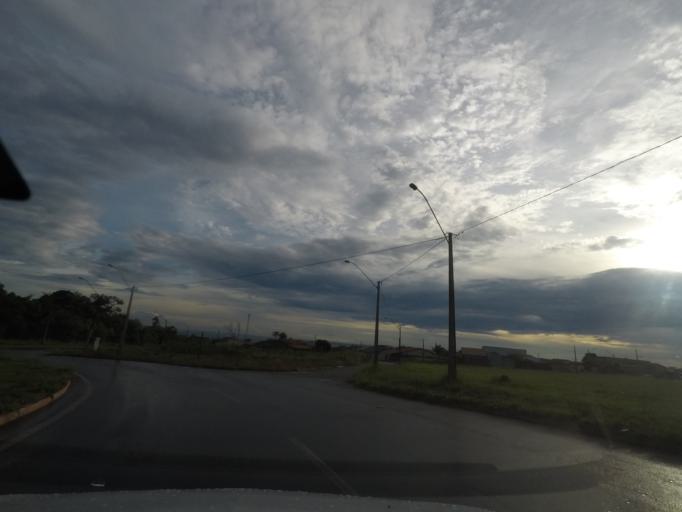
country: BR
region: Goias
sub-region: Goiania
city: Goiania
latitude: -16.7518
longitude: -49.3772
